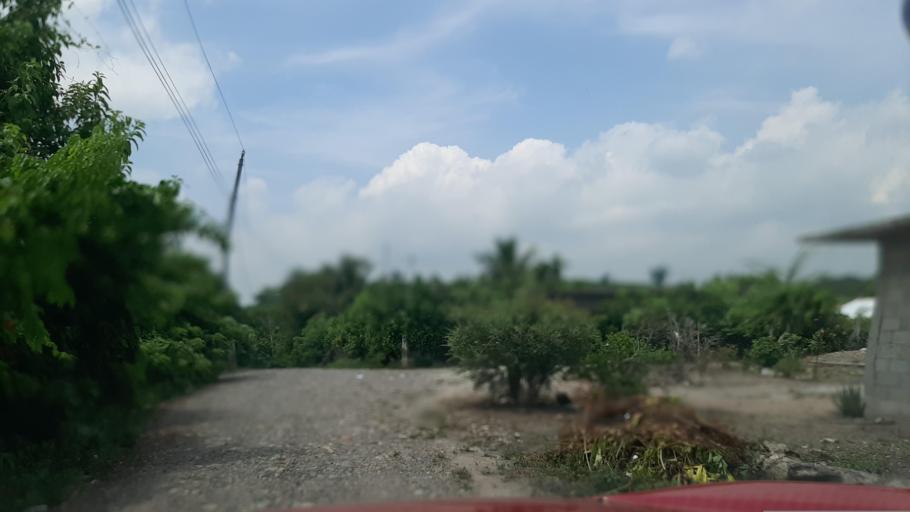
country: MX
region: Veracruz
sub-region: Papantla
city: Polutla
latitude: 20.4479
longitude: -97.2431
